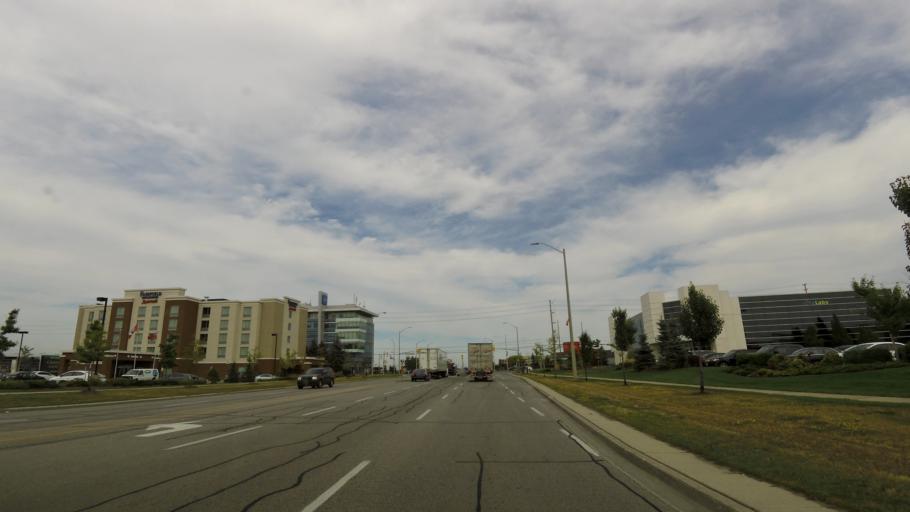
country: CA
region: Ontario
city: Mississauga
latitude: 43.6361
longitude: -79.6953
